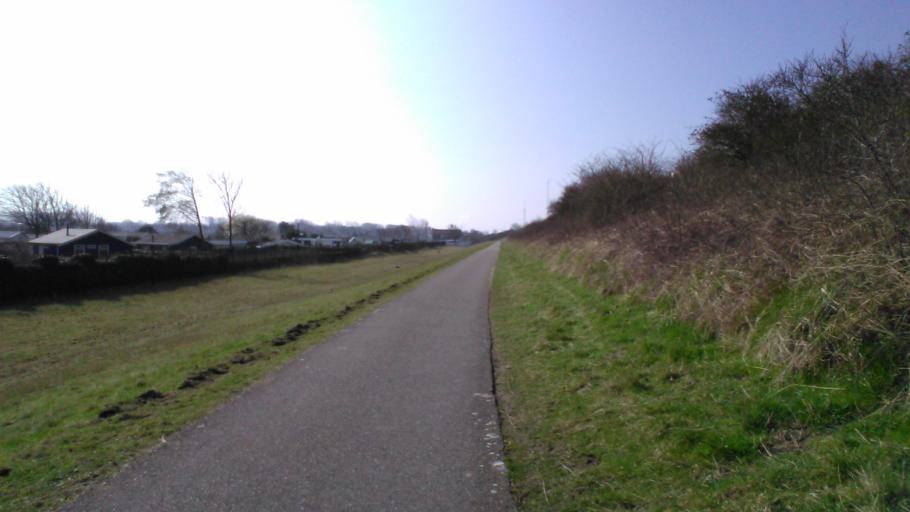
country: NL
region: South Holland
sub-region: Gemeente Rotterdam
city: Hoek van Holland
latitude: 51.9959
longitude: 4.1293
